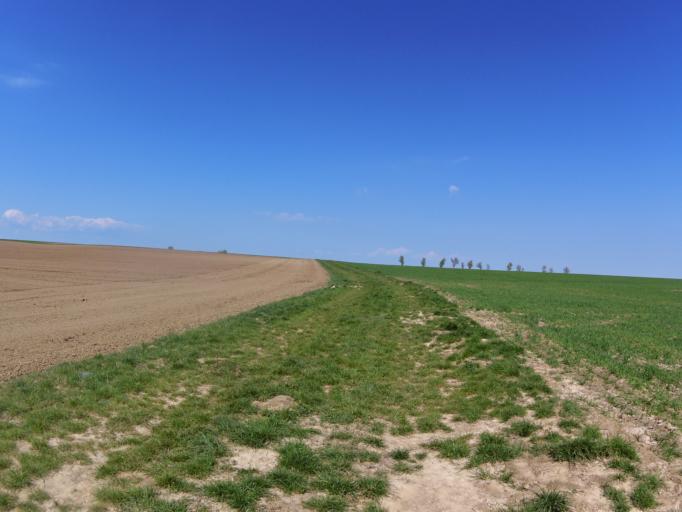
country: DE
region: Bavaria
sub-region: Regierungsbezirk Unterfranken
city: Oberpleichfeld
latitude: 49.8484
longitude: 10.0760
